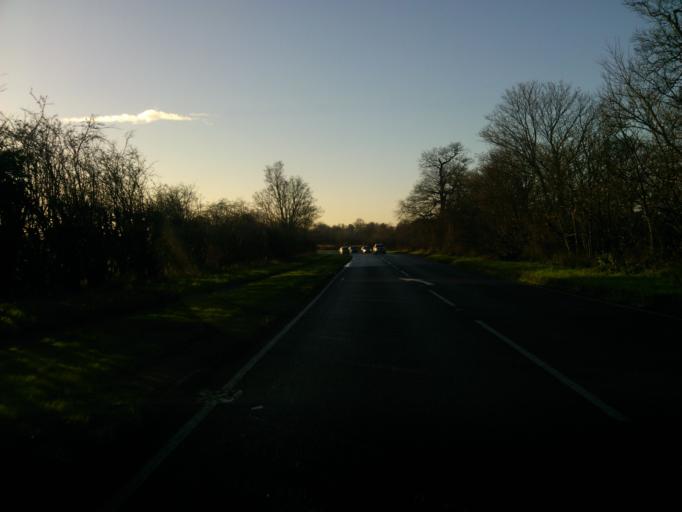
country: GB
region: England
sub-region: Essex
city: Saint Osyth
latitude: 51.8111
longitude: 1.0736
